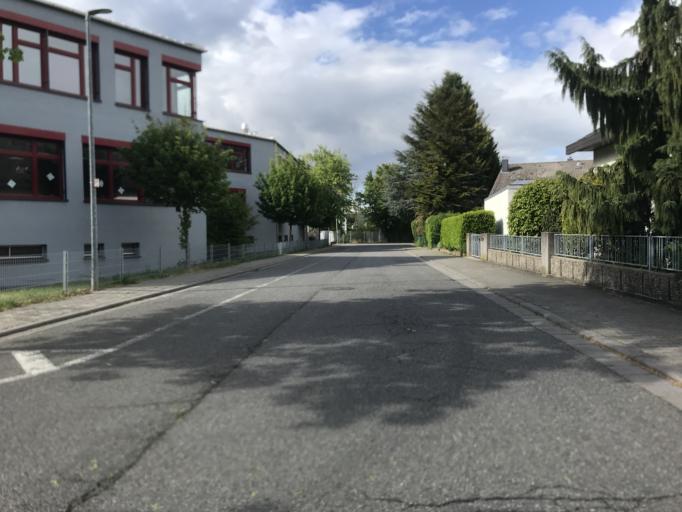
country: DE
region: Rheinland-Pfalz
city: Nieder-Olm
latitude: 49.9011
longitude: 8.1967
